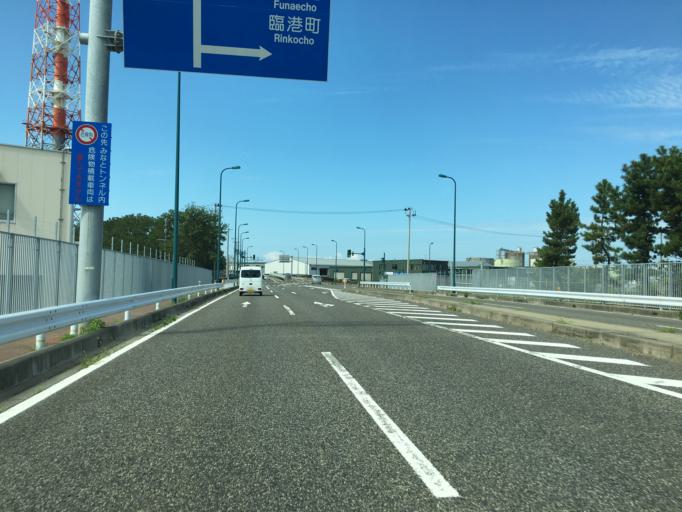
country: JP
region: Niigata
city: Niigata-shi
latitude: 37.9470
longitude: 139.0831
